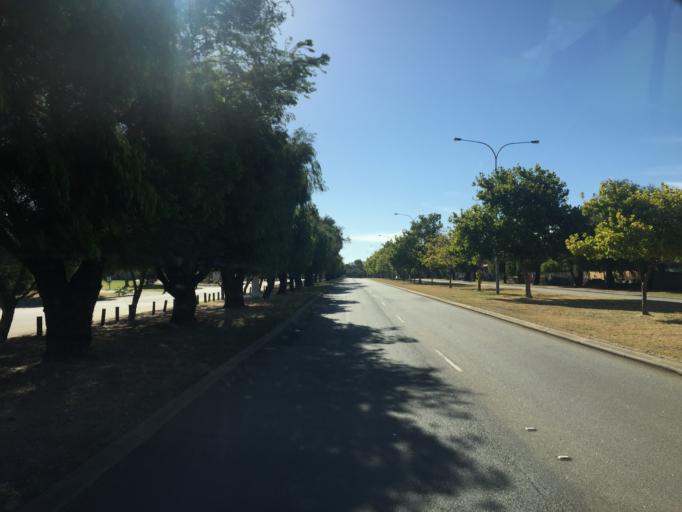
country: AU
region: Western Australia
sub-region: Canning
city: Queens Park
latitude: -31.9954
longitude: 115.9515
